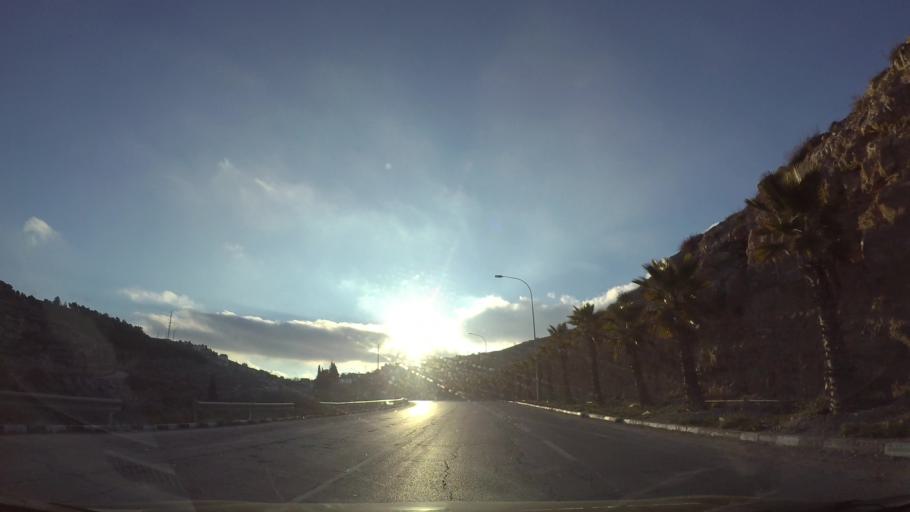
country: JO
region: Ma'an
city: Petra
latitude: 30.5211
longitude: 35.5470
